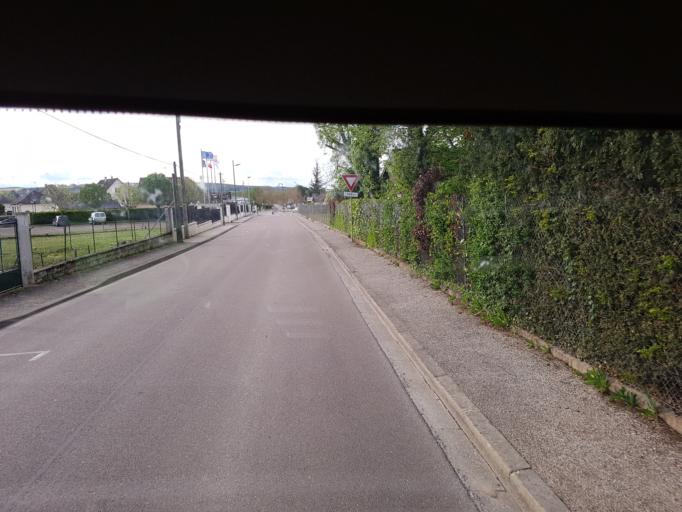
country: FR
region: Bourgogne
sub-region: Departement de l'Yonne
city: Chablis
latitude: 47.8147
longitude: 3.7950
